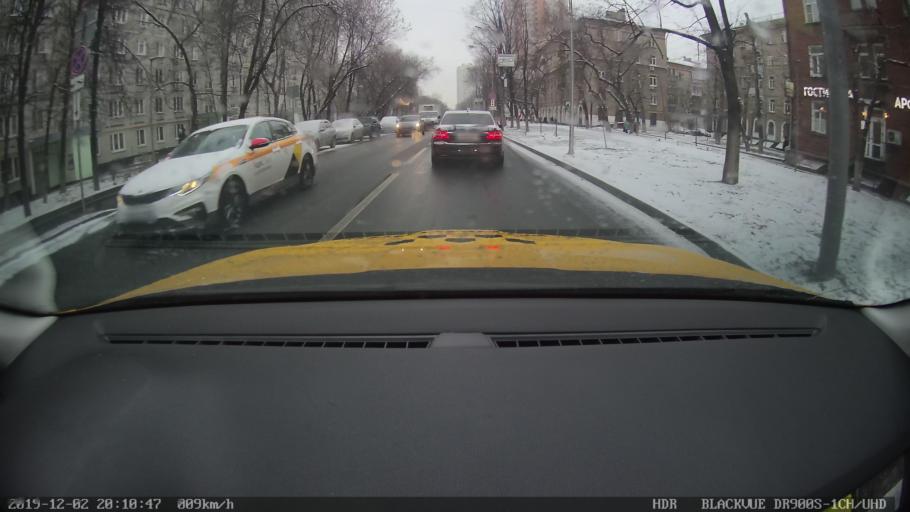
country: RU
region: Moscow
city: Novokuz'minki
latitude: 55.7145
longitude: 37.7904
